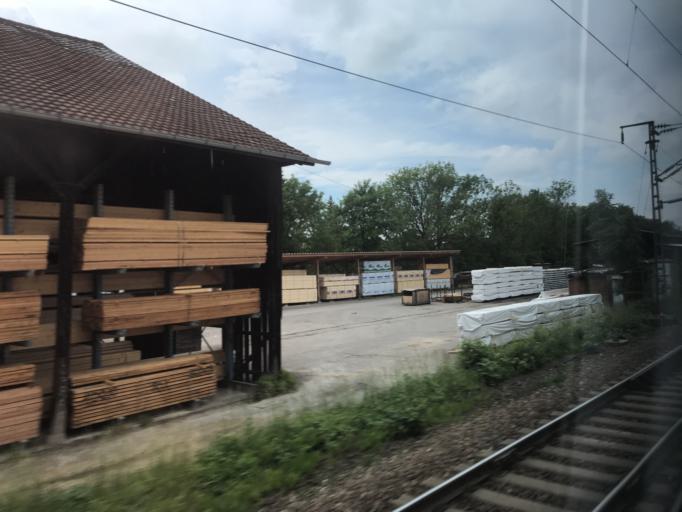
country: DE
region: Baden-Wuerttemberg
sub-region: Regierungsbezirk Stuttgart
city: Eislingen
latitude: 48.6951
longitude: 9.7111
